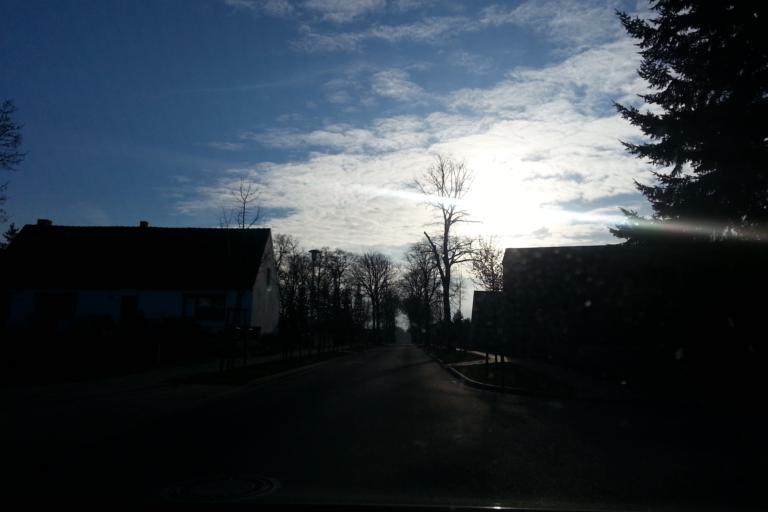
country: DE
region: Mecklenburg-Vorpommern
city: Ferdinandshof
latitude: 53.6440
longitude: 13.8607
